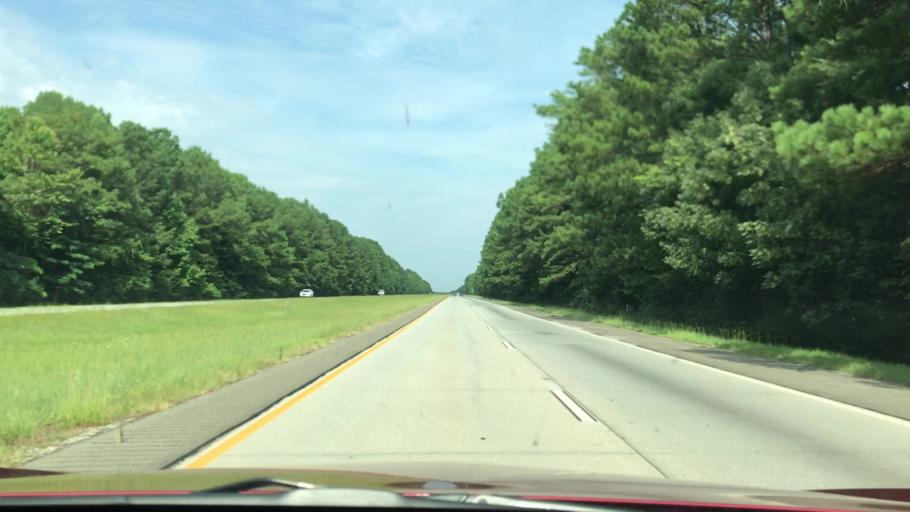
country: US
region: Georgia
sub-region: Warren County
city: Firing Range
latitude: 33.5039
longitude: -82.7358
